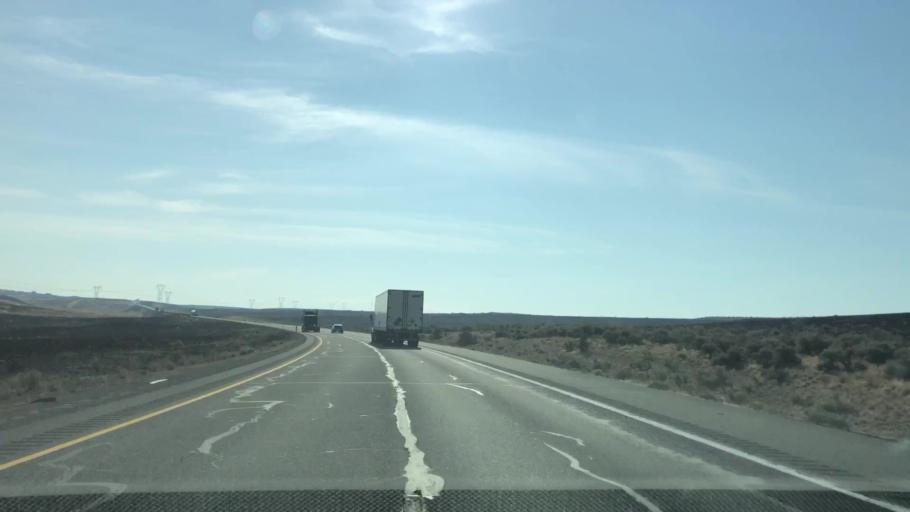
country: US
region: Washington
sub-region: Kittitas County
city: Kittitas
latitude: 46.9449
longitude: -120.2412
